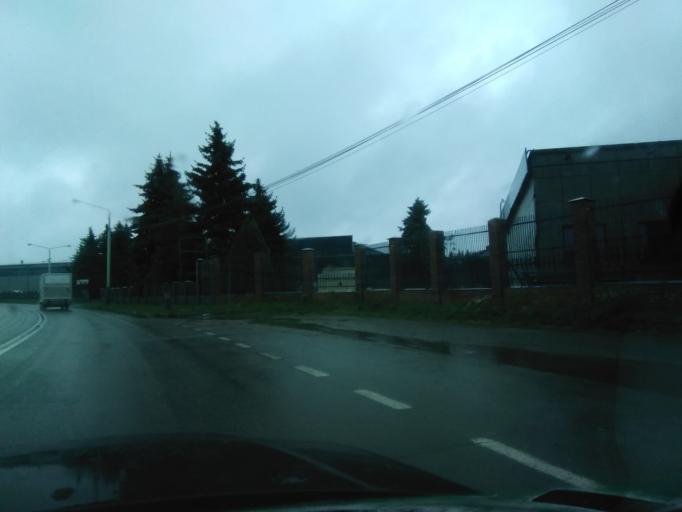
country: PL
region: Subcarpathian Voivodeship
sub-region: Powiat debicki
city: Debica
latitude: 50.0544
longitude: 21.3906
